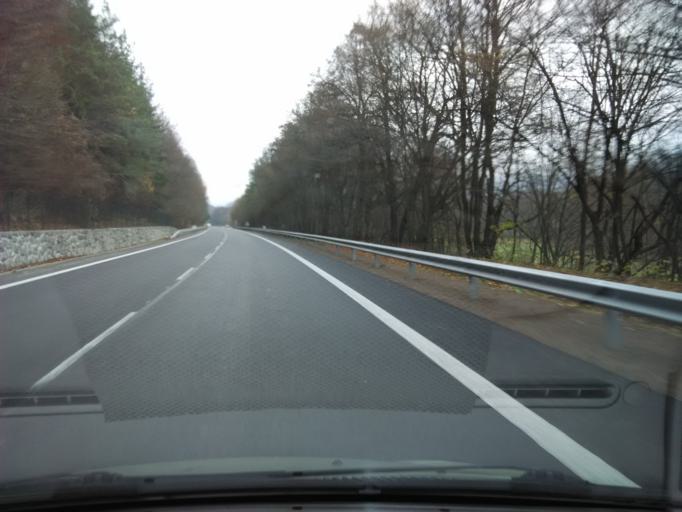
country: SK
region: Banskobystricky
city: Ziar nad Hronom
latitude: 48.6200
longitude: 18.8958
